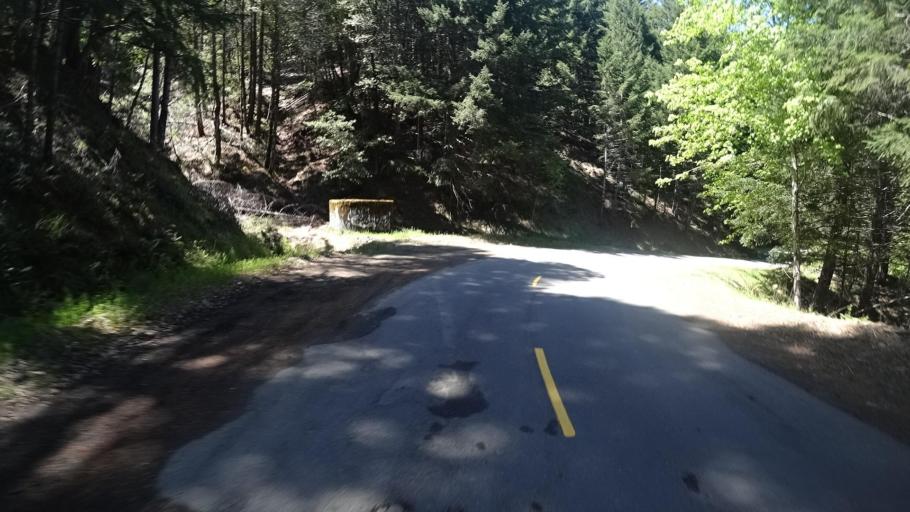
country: US
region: California
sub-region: Humboldt County
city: Rio Dell
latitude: 40.3182
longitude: -124.0617
